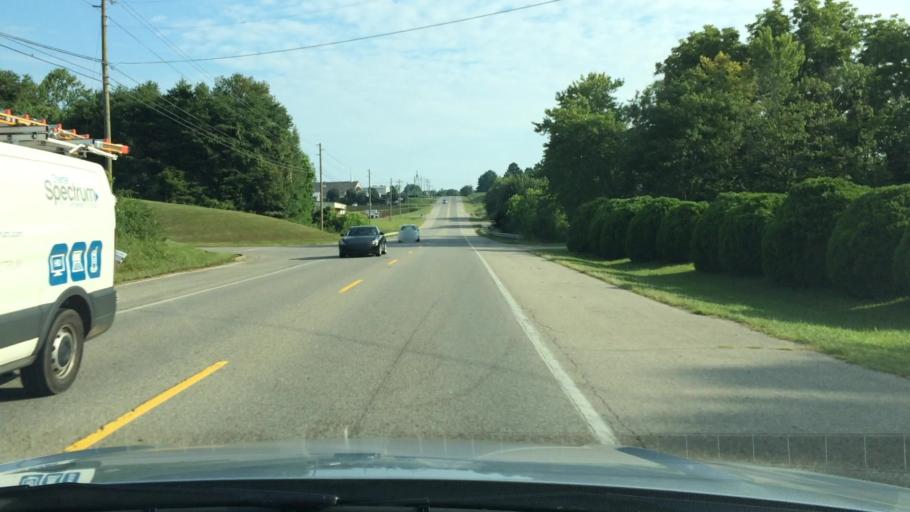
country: US
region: Tennessee
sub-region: Blount County
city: Louisville
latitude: 35.7480
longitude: -84.0443
